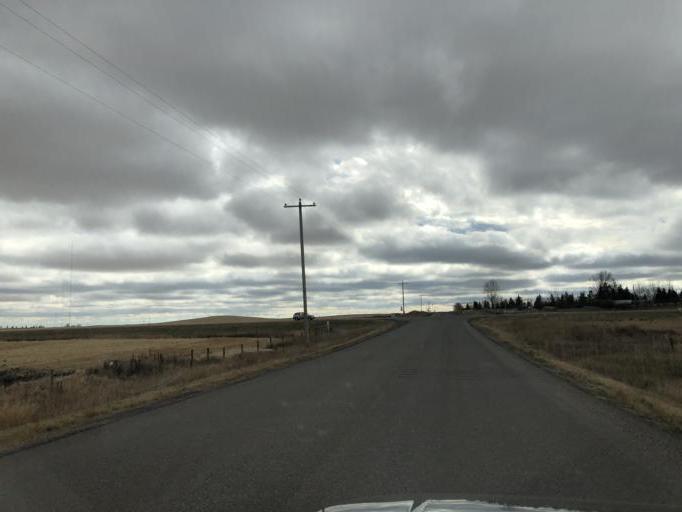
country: CA
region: Alberta
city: Chestermere
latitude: 50.9083
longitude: -113.8830
